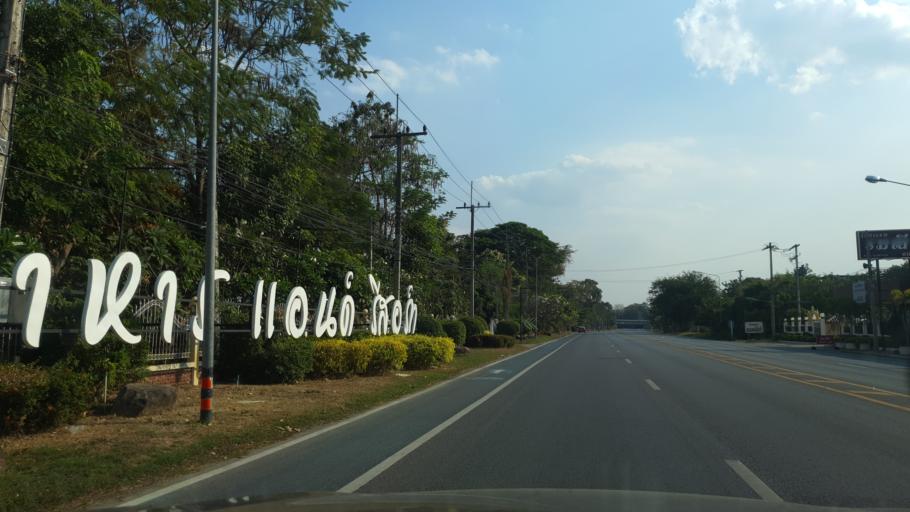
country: TH
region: Tak
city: Tak
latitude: 16.8612
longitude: 99.1212
